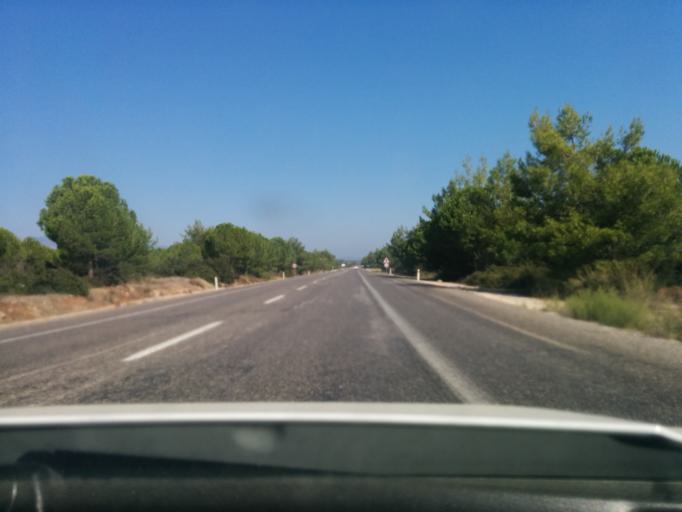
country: TR
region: Mugla
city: Esen
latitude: 36.3774
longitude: 29.3223
